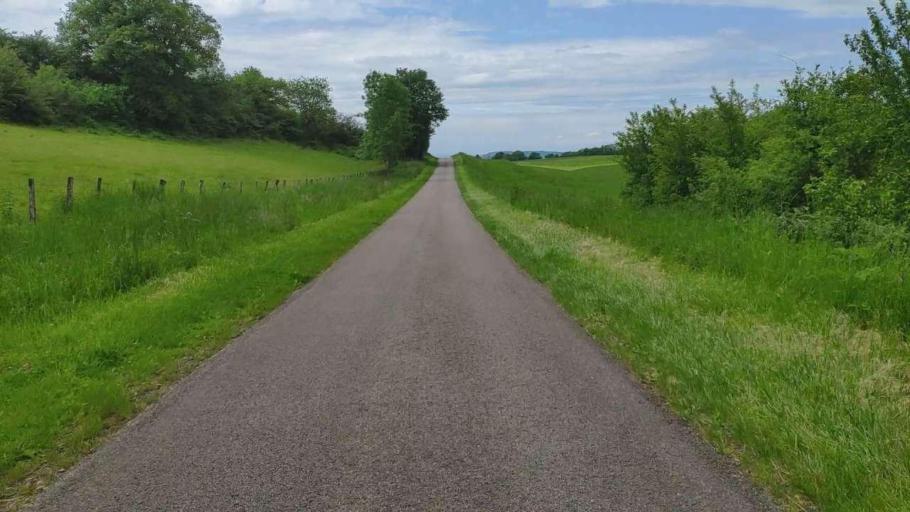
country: FR
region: Franche-Comte
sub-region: Departement du Jura
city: Poligny
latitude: 46.7698
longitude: 5.6499
